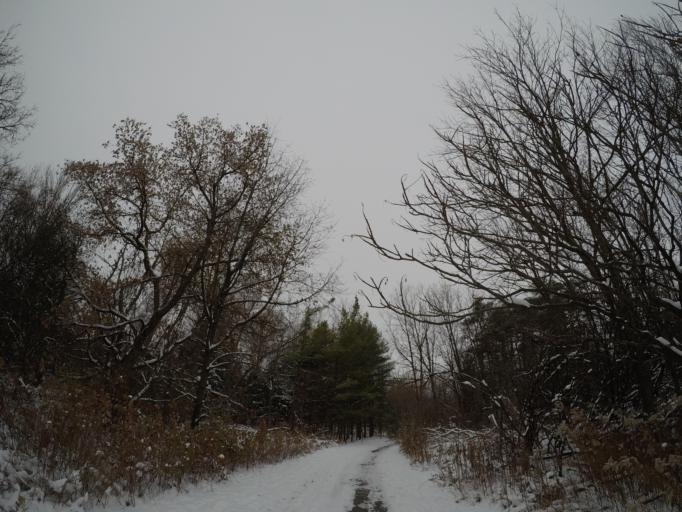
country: CA
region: Ontario
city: Waterloo
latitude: 43.4858
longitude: -80.5059
